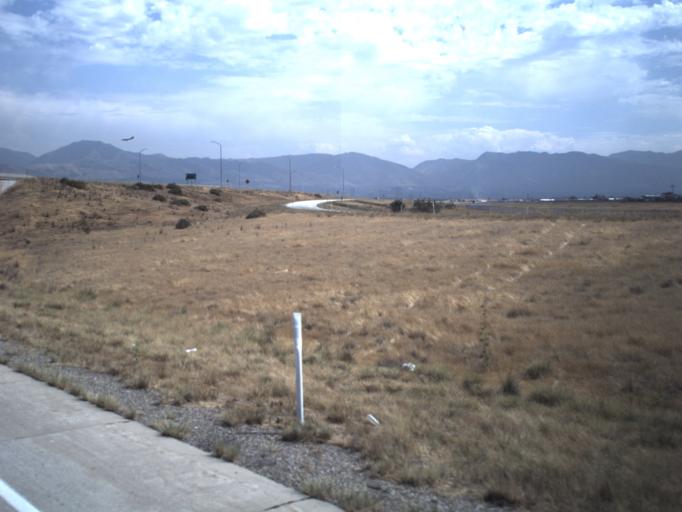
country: US
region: Utah
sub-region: Salt Lake County
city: West Valley City
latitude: 40.7630
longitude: -111.9836
